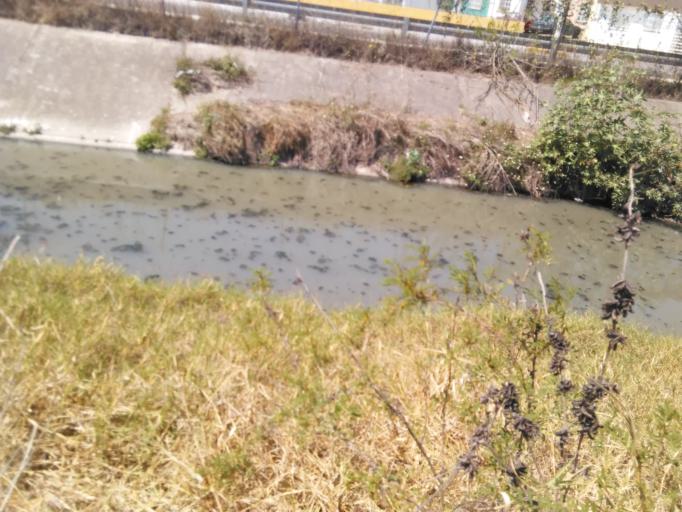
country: MX
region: Nayarit
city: Tepic
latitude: 21.4948
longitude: -104.8734
